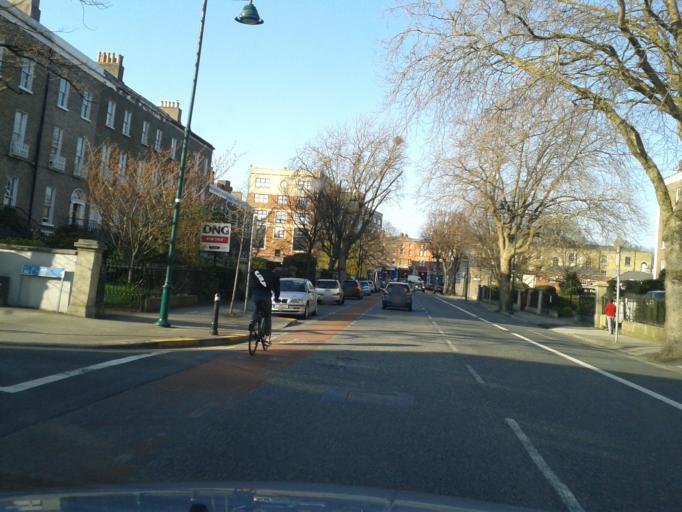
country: IE
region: Leinster
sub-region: Dublin City
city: Dublin
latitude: 53.3311
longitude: -6.2442
